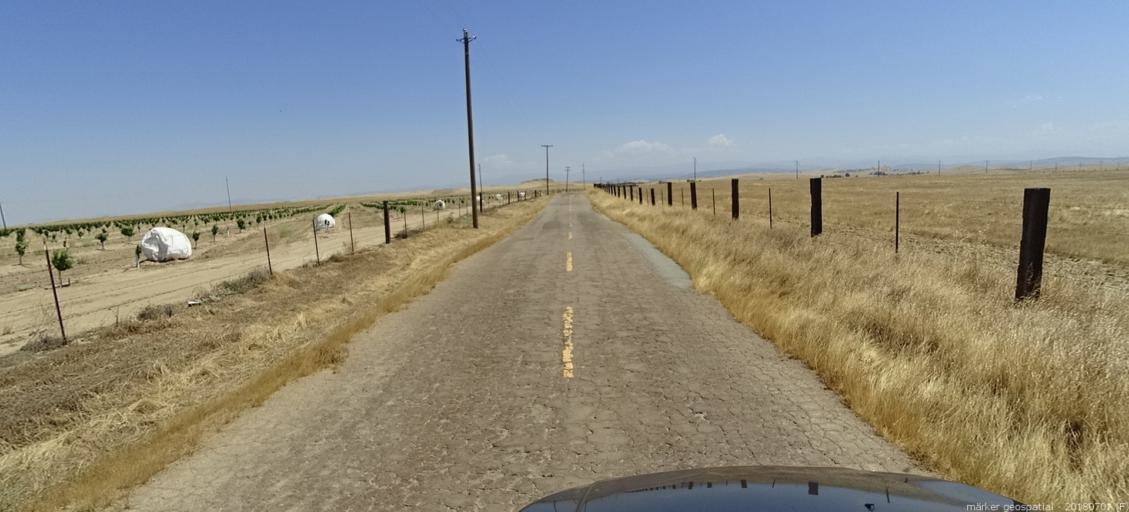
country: US
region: California
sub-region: Madera County
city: Madera Acres
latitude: 37.0951
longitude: -120.0072
